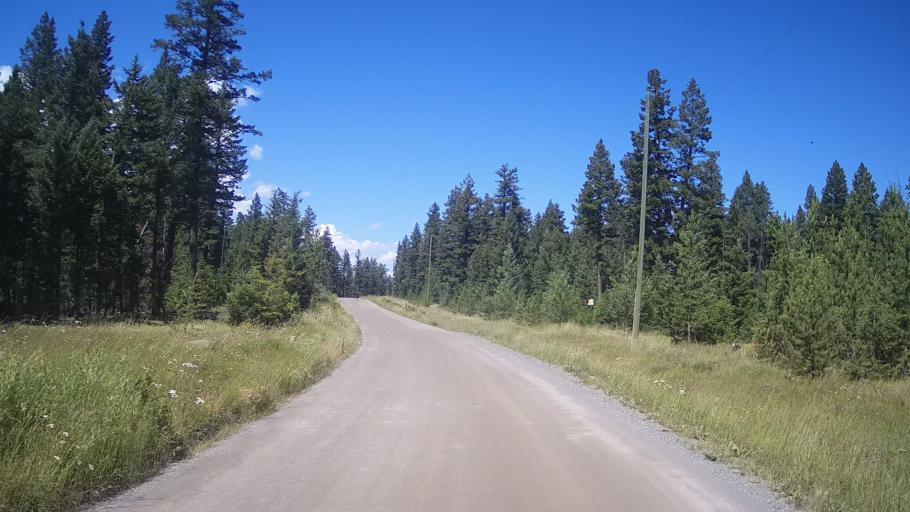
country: CA
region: British Columbia
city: Cache Creek
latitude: 51.2110
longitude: -121.6004
